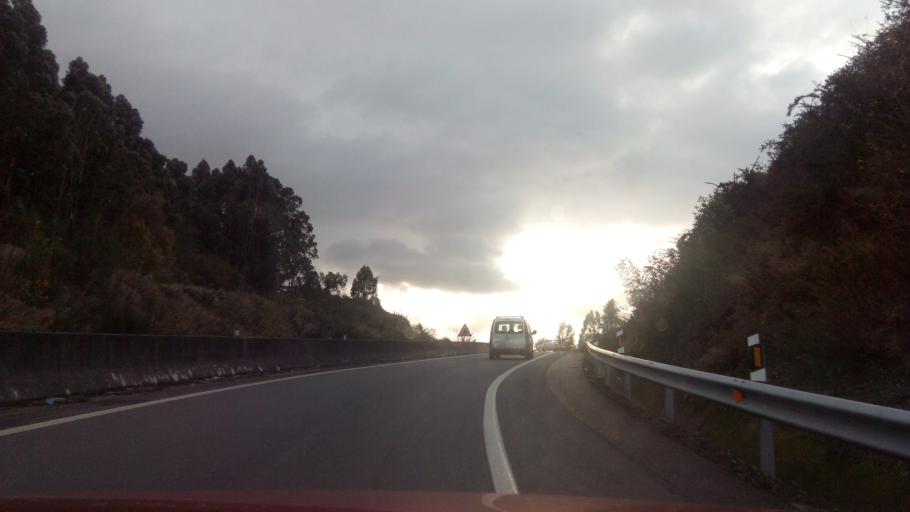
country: ES
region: Galicia
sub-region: Provincia de Pontevedra
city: Vigo
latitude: 42.2105
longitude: -8.6642
